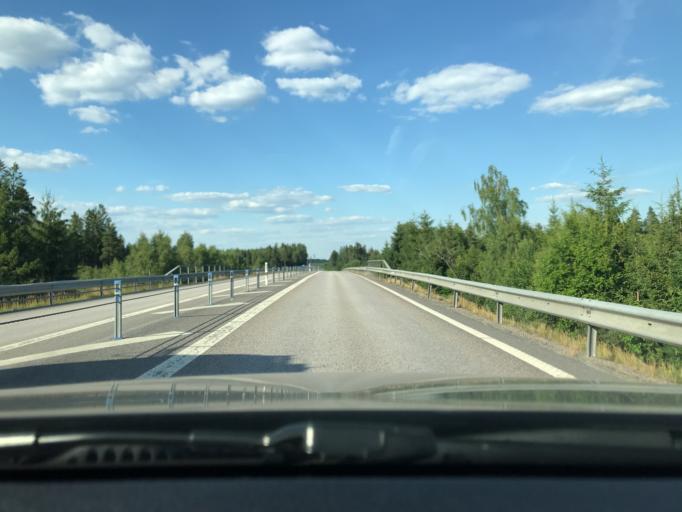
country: SE
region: Kronoberg
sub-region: Alvesta Kommun
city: Vislanda
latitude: 56.7477
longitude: 14.5135
